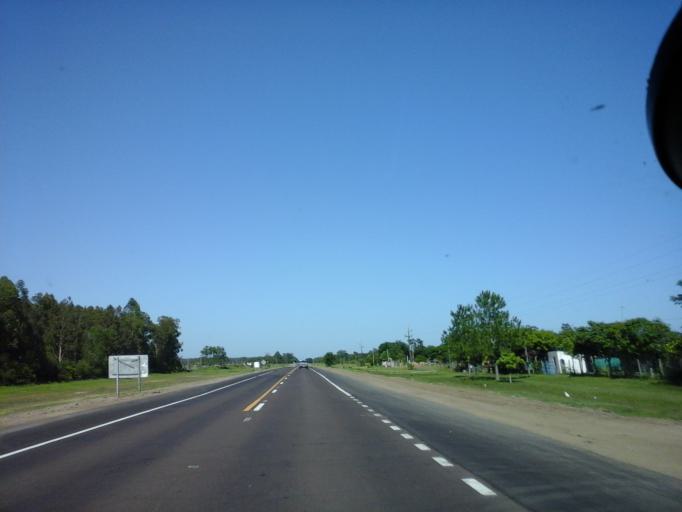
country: AR
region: Corrientes
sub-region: Departamento de San Cosme
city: San Cosme
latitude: -27.3675
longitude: -58.3676
